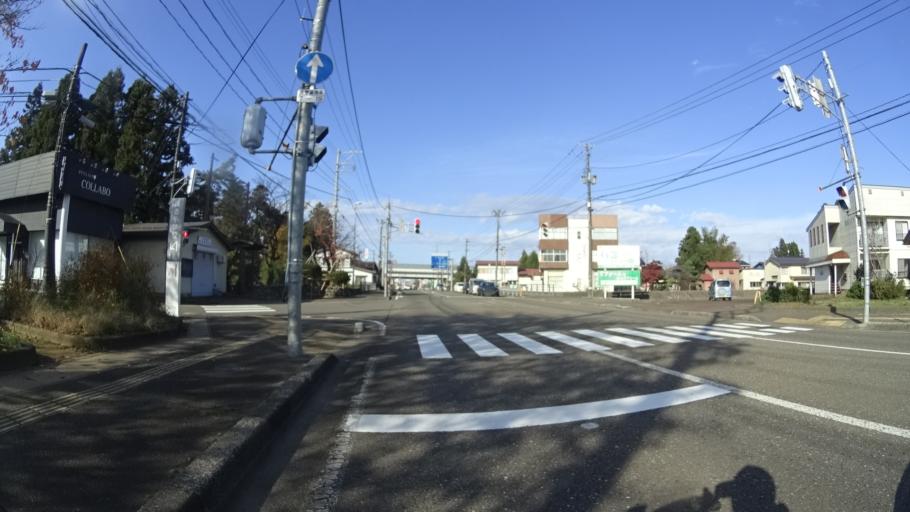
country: JP
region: Niigata
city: Joetsu
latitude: 37.1411
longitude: 138.2405
